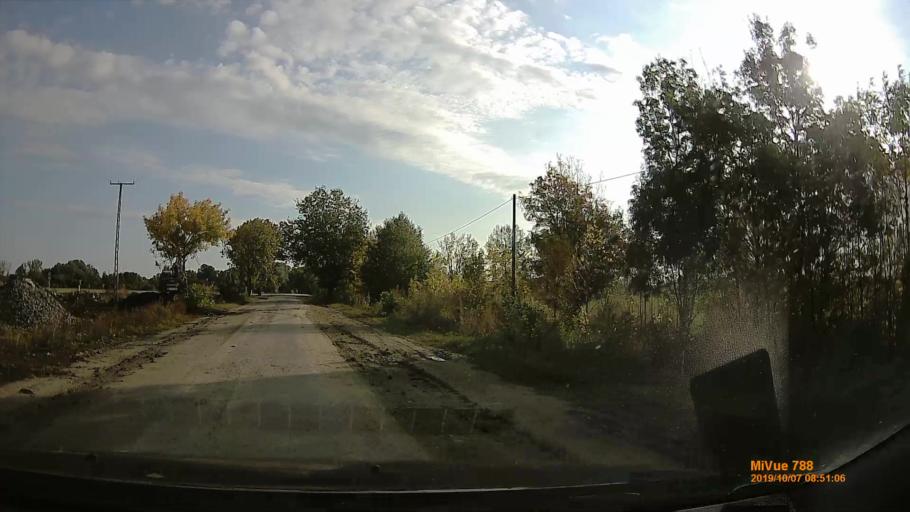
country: HU
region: Bekes
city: Szarvas
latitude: 46.8199
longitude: 20.5228
